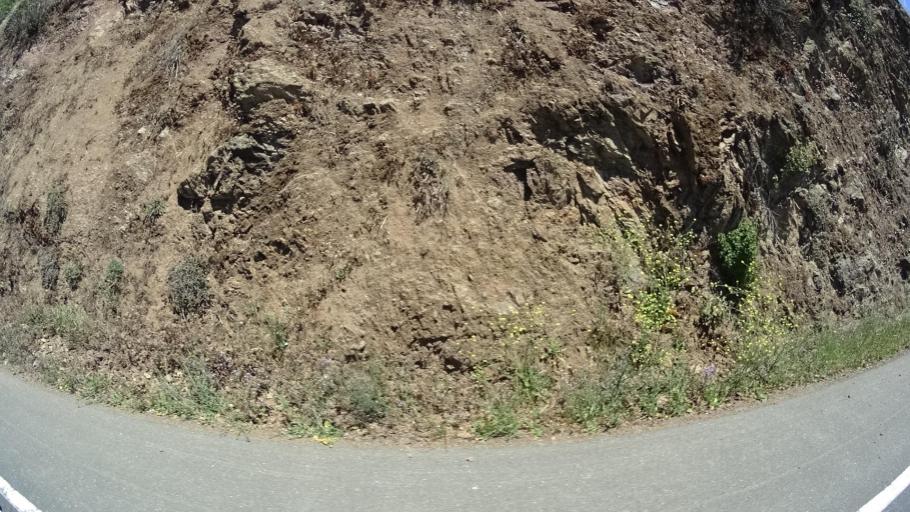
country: US
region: California
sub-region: Lake County
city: Lucerne
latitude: 39.0488
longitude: -122.7787
